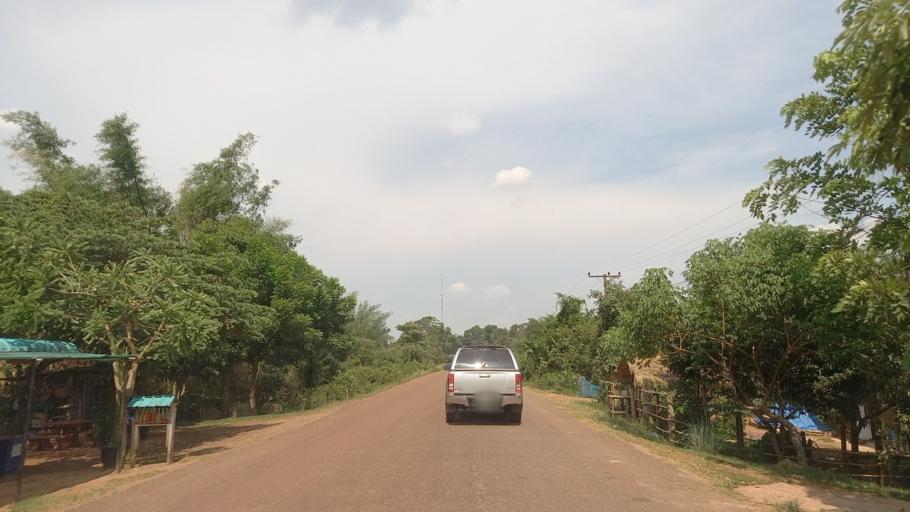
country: LA
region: Bolikhamxai
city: Muang Pakxan
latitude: 18.4281
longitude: 103.7137
